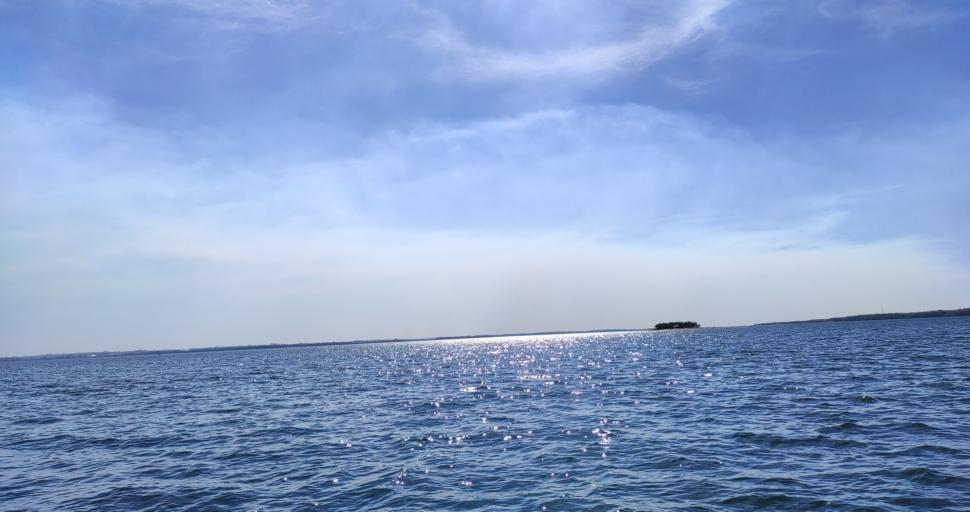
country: AR
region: Misiones
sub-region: Departamento de Capital
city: Posadas
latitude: -27.3435
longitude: -55.9372
